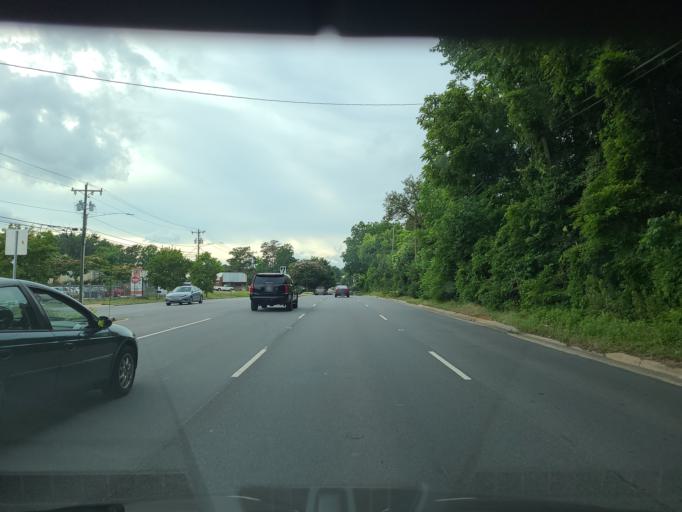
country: US
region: North Carolina
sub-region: Mecklenburg County
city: Charlotte
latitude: 35.2304
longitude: -80.9193
